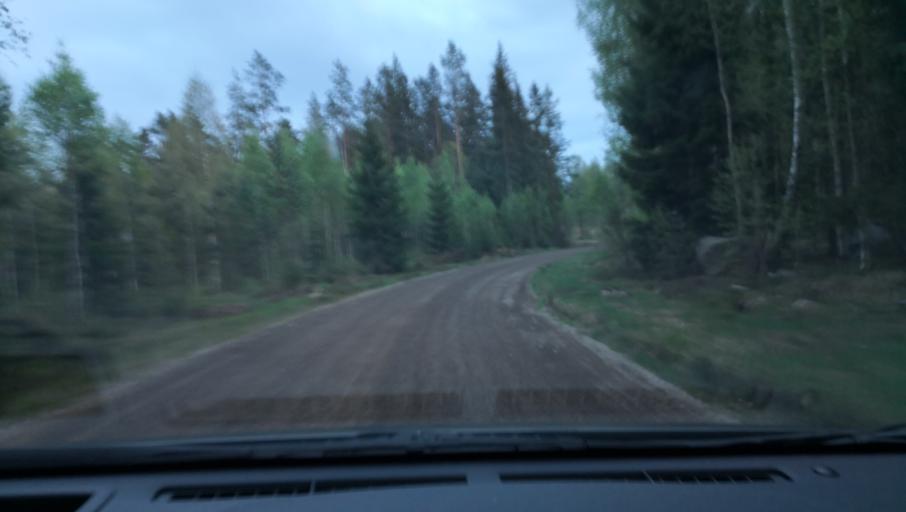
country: SE
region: Vaestmanland
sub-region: Skinnskattebergs Kommun
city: Skinnskatteberg
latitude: 59.7047
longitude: 15.5147
